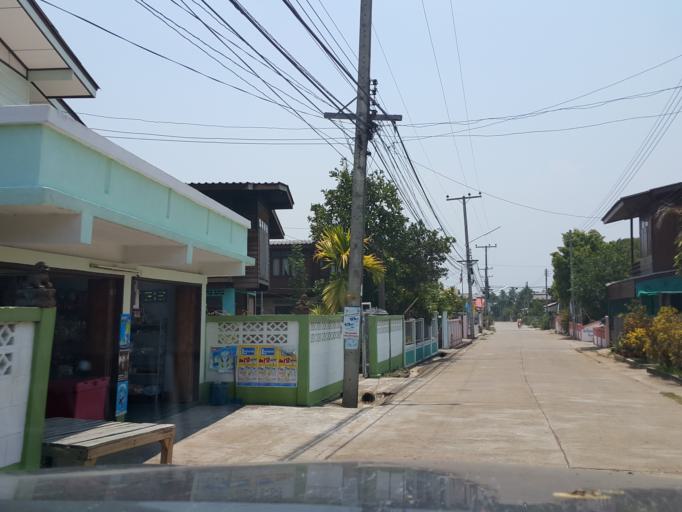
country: TH
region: Lampang
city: Thoen
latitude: 17.6389
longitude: 99.2596
